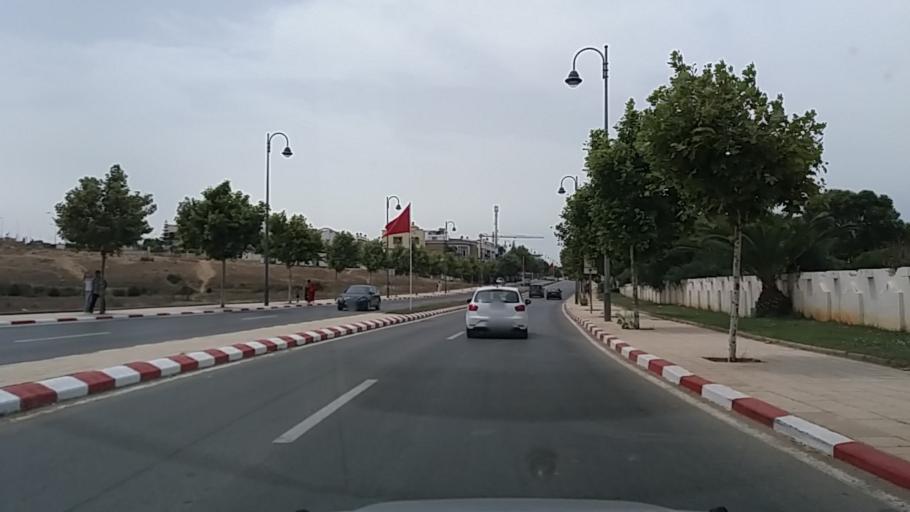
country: MA
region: Tanger-Tetouan
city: Asilah
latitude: 35.4733
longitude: -6.0269
